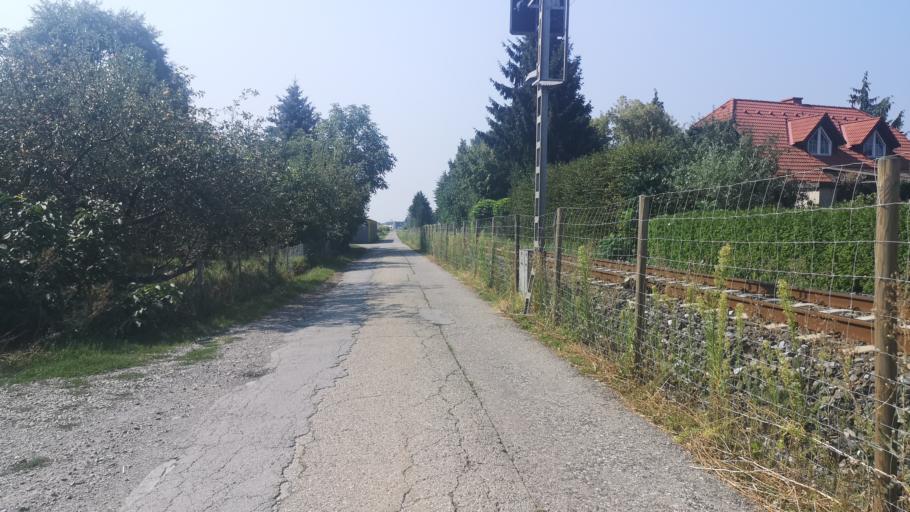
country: AT
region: Styria
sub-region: Politischer Bezirk Graz-Umgebung
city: Seiersberg
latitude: 47.0094
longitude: 15.4026
